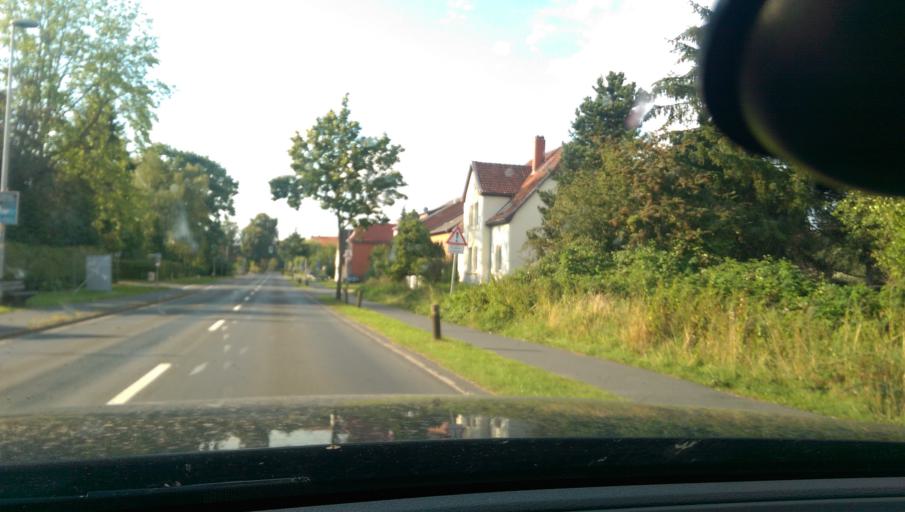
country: DE
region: Lower Saxony
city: Neustadt am Rubenberge
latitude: 52.5079
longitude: 9.4552
